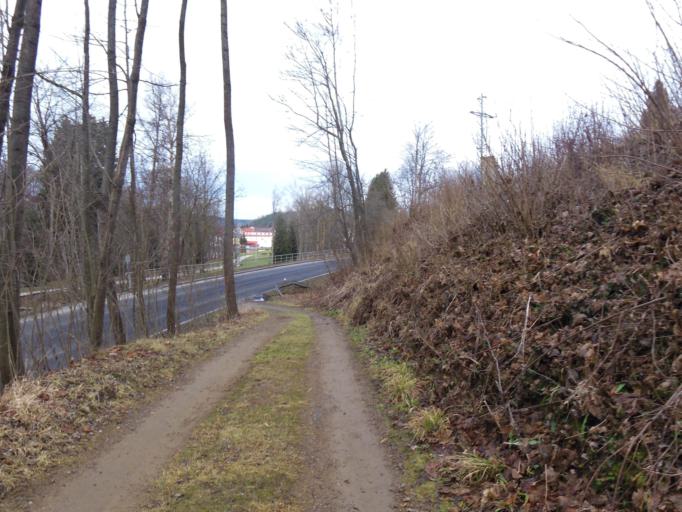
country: CZ
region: Plzensky
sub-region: Okres Klatovy
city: Susice
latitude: 49.2257
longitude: 13.5180
